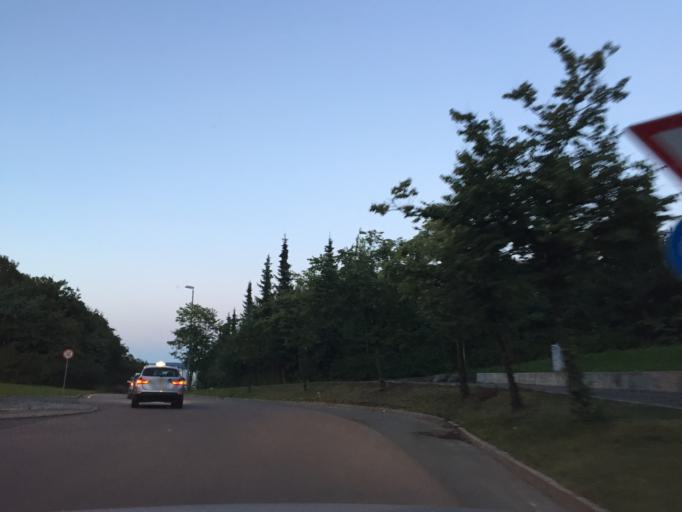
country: NO
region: Akershus
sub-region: Baerum
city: Lysaker
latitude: 59.9253
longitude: 10.6486
